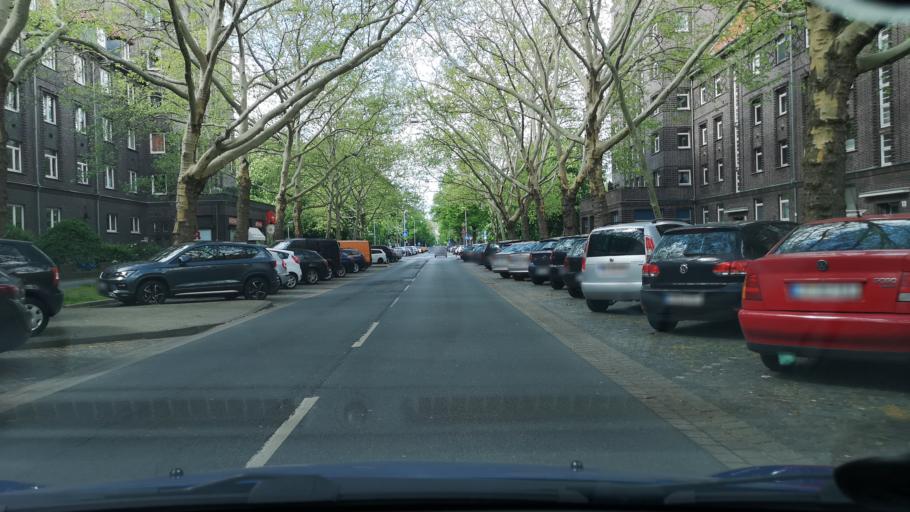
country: DE
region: Lower Saxony
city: Hannover
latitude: 52.3581
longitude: 9.7620
